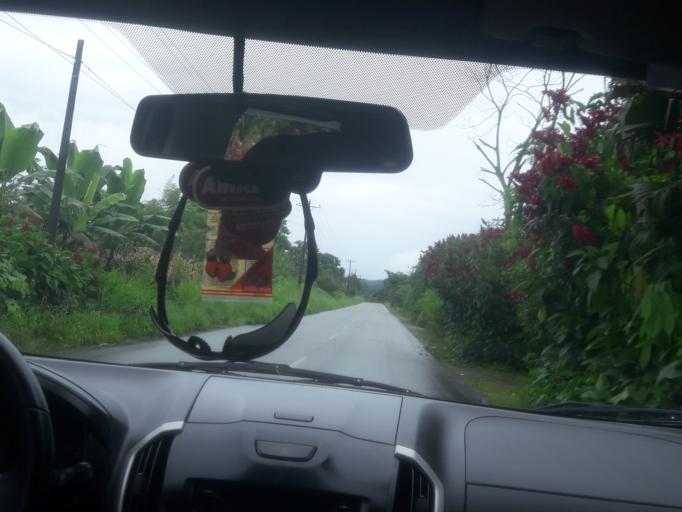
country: EC
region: Napo
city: Tena
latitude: -1.0307
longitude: -77.7435
